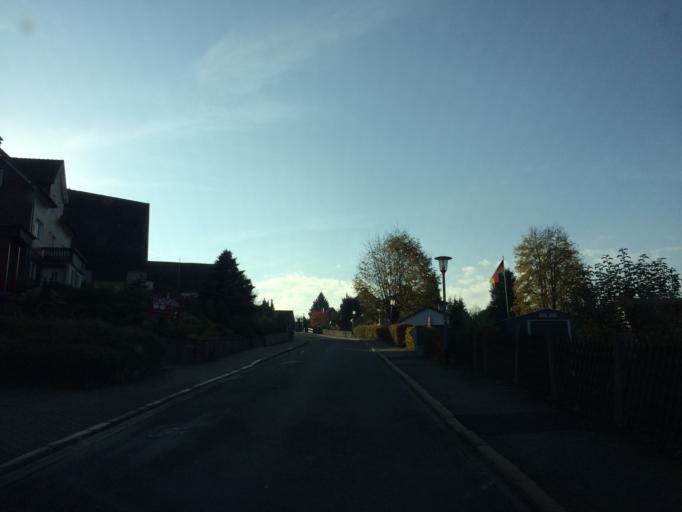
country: DE
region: Lower Saxony
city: Braunlage
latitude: 51.7256
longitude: 10.6085
